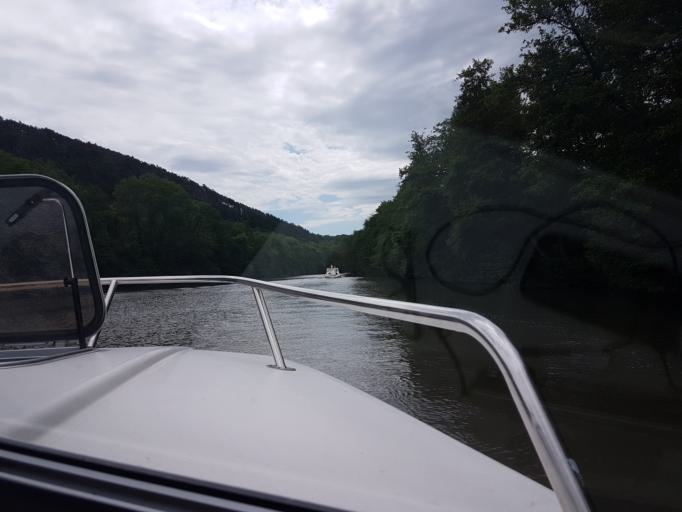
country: FR
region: Bourgogne
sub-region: Departement de la Nievre
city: Clamecy
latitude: 47.4748
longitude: 3.5271
